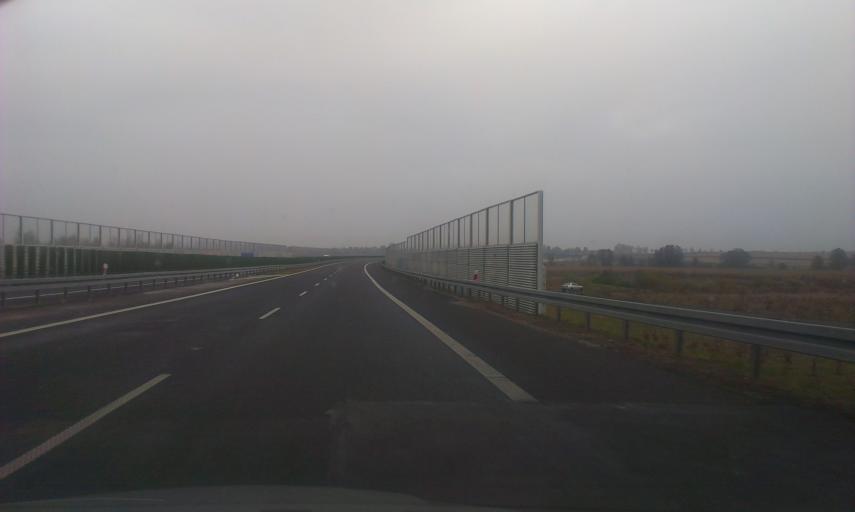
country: PL
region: Greater Poland Voivodeship
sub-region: Powiat poznanski
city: Rokietnica
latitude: 52.5117
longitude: 16.7841
